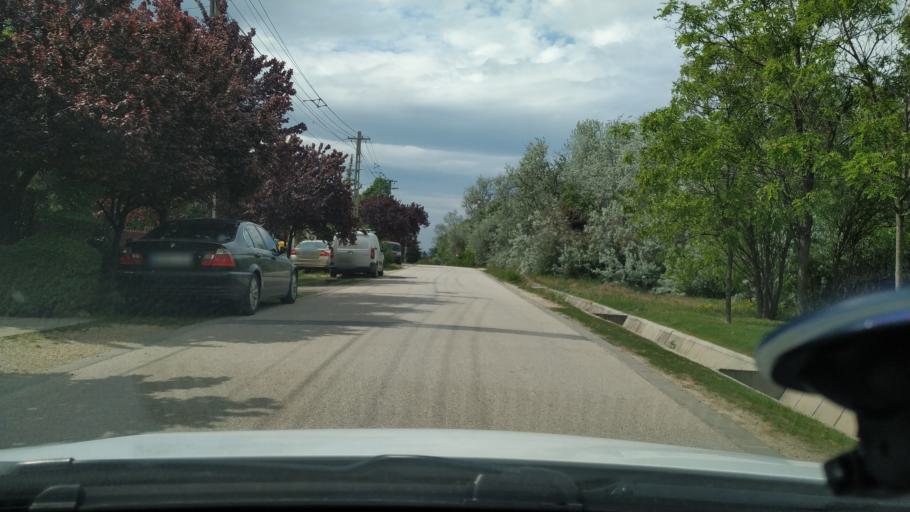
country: HU
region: Pest
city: Dunaharaszti
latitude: 47.3685
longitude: 19.0970
